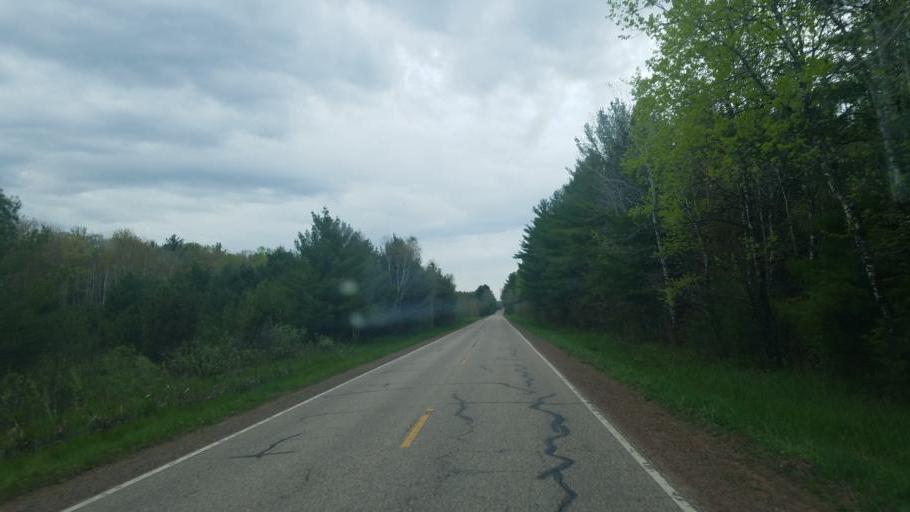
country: US
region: Wisconsin
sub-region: Wood County
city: Marshfield
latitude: 44.5310
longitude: -90.2996
